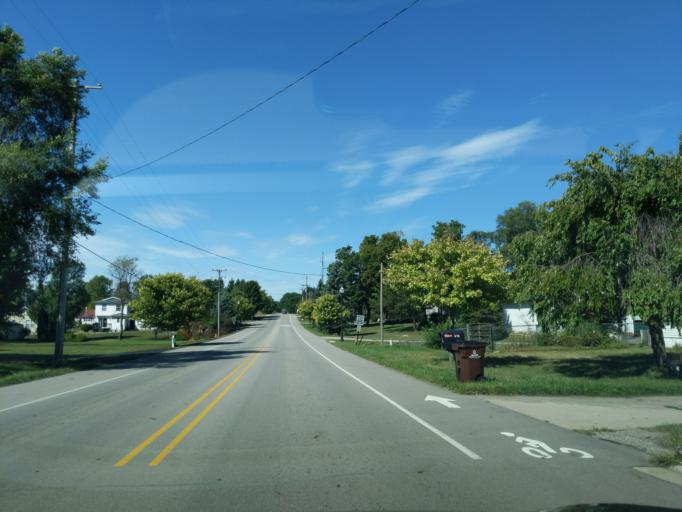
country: US
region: Michigan
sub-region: Eaton County
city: Potterville
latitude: 42.6257
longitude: -84.7484
